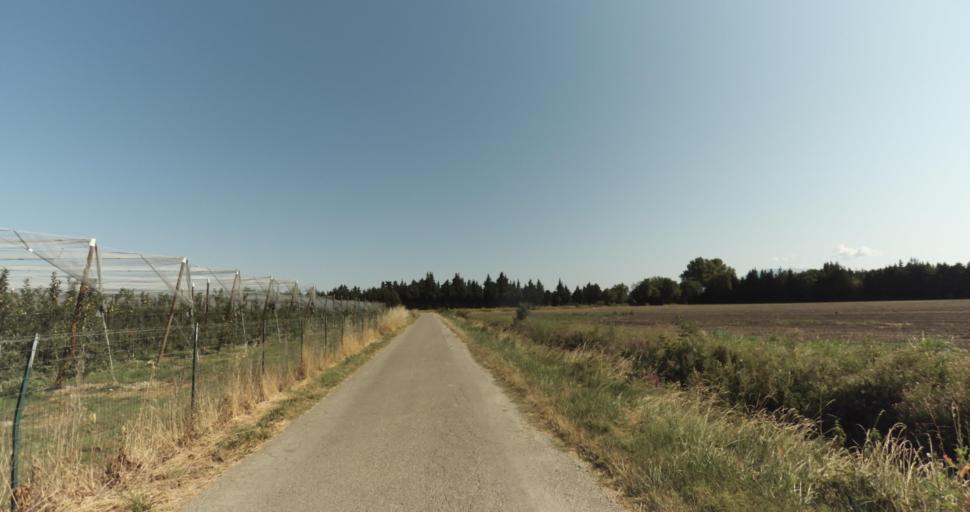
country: FR
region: Provence-Alpes-Cote d'Azur
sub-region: Departement du Vaucluse
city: Althen-des-Paluds
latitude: 44.0069
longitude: 4.9736
